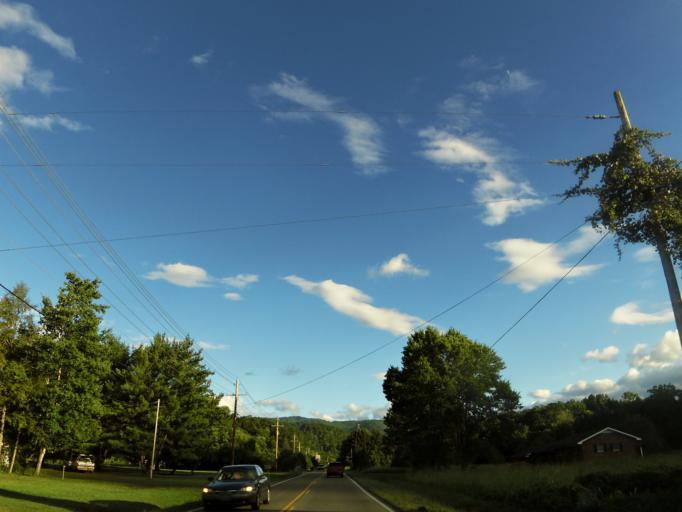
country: US
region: Tennessee
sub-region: Cocke County
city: Newport
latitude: 35.8576
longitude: -83.2189
